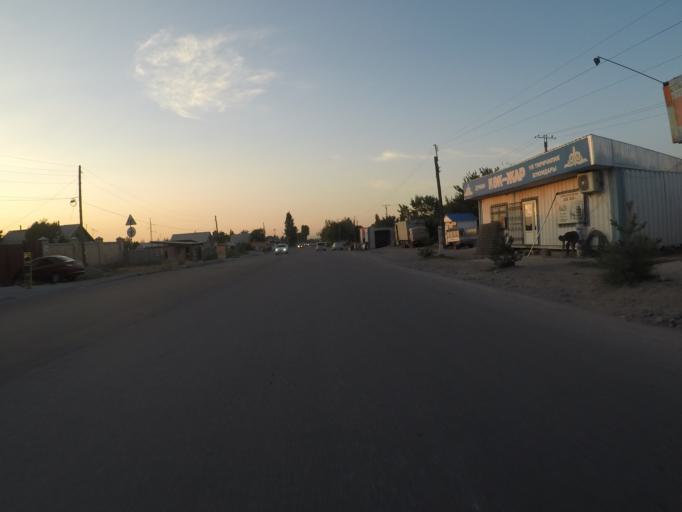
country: KG
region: Chuy
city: Lebedinovka
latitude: 42.8051
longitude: 74.6479
